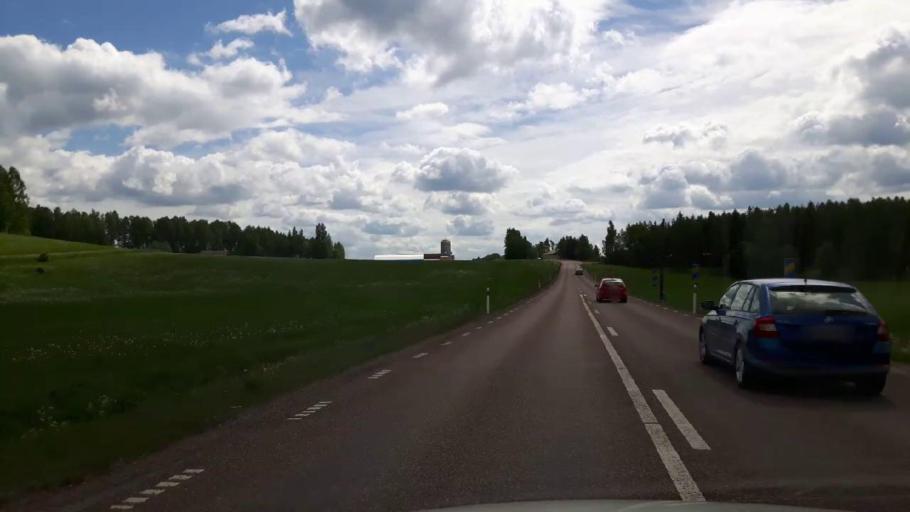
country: SE
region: Dalarna
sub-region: Saters Kommun
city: Saeter
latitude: 60.4321
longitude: 15.8307
